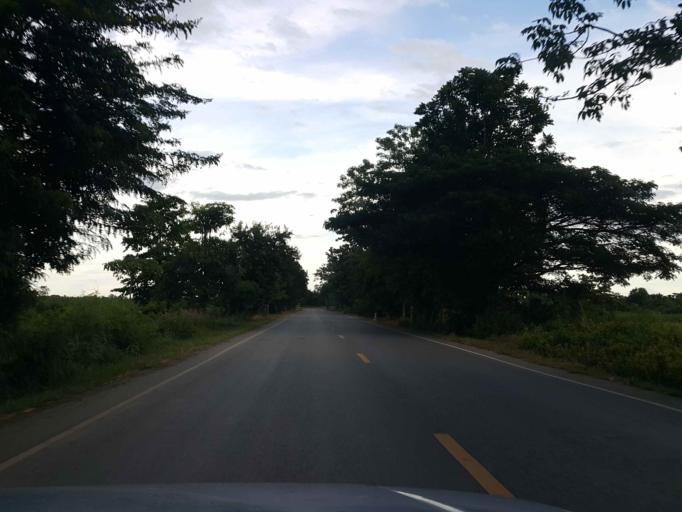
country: TH
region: Sukhothai
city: Sawankhalok
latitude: 17.3753
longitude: 99.7395
